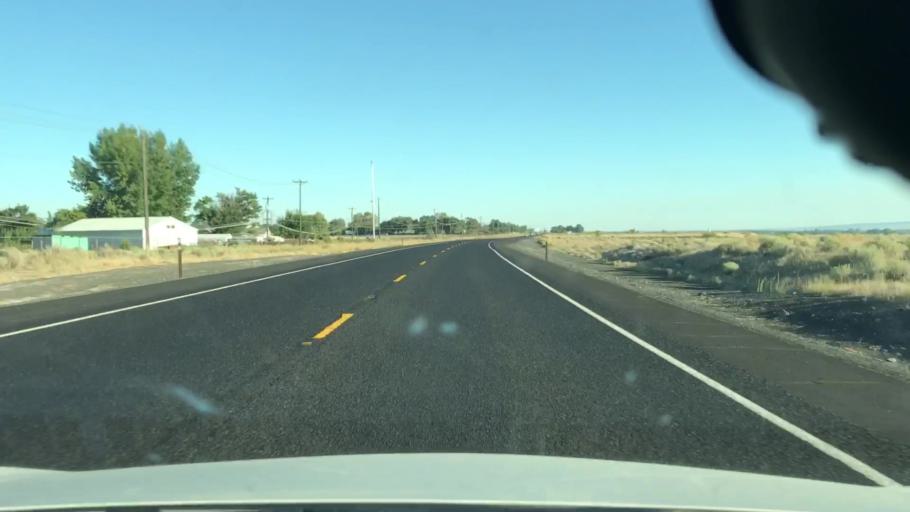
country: US
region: Washington
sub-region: Grant County
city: Moses Lake North
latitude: 47.1761
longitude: -119.3315
